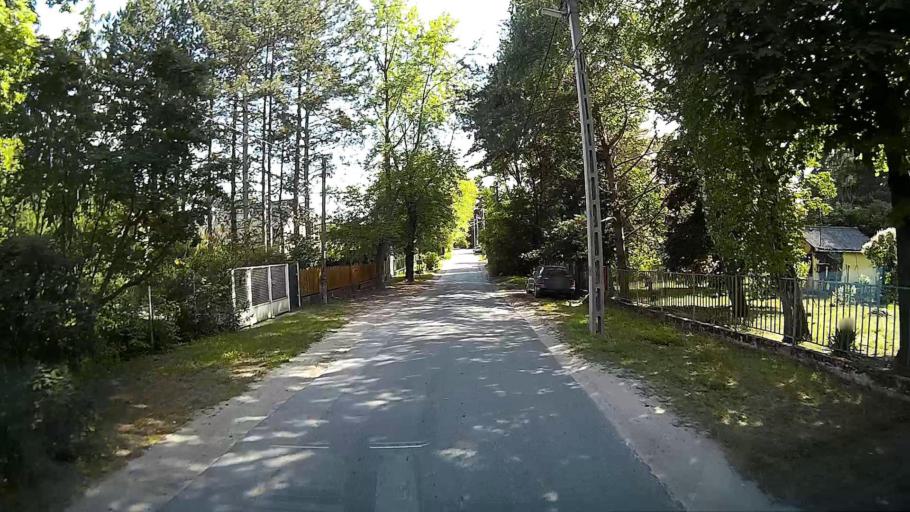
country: HU
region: Pest
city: Leanyfalu
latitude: 47.7148
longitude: 19.1094
